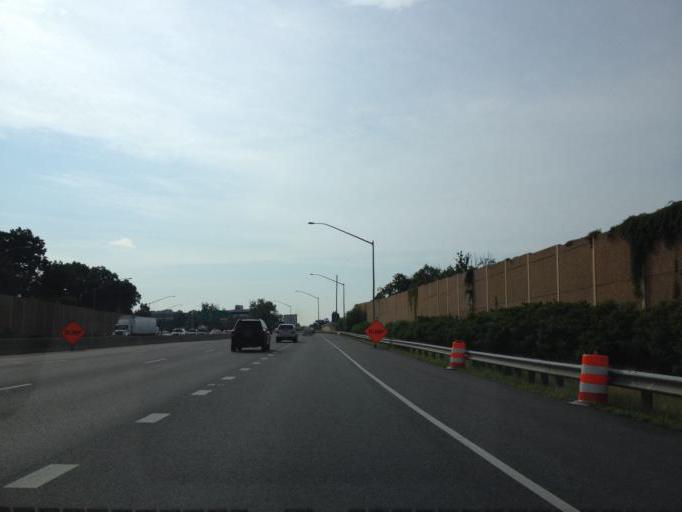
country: US
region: Maryland
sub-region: Baltimore County
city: Lutherville
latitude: 39.4138
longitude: -76.6221
